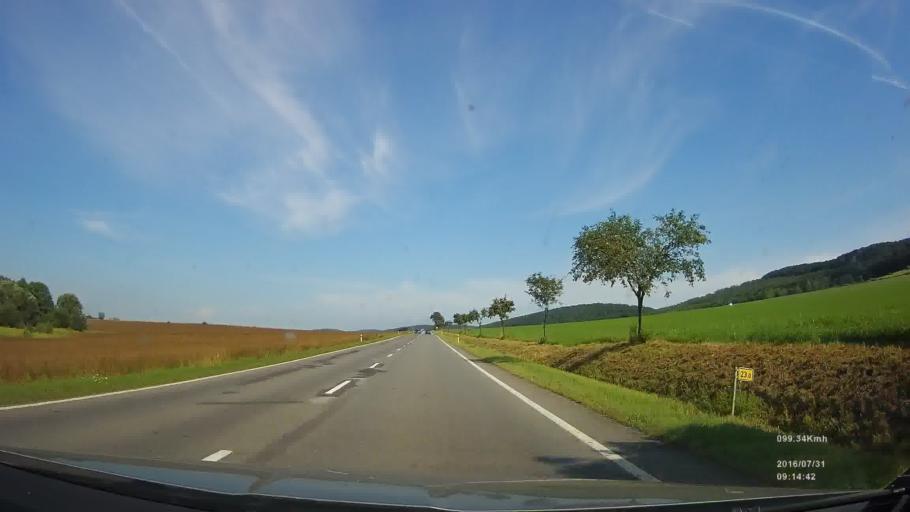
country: SK
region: Presovsky
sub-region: Okres Bardejov
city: Bardejov
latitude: 49.2245
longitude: 21.2903
